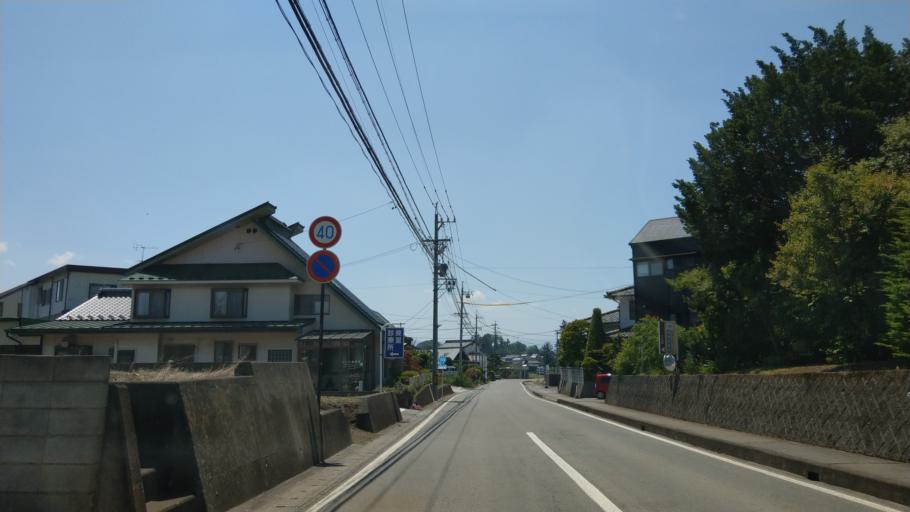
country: JP
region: Nagano
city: Komoro
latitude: 36.2906
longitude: 138.4404
